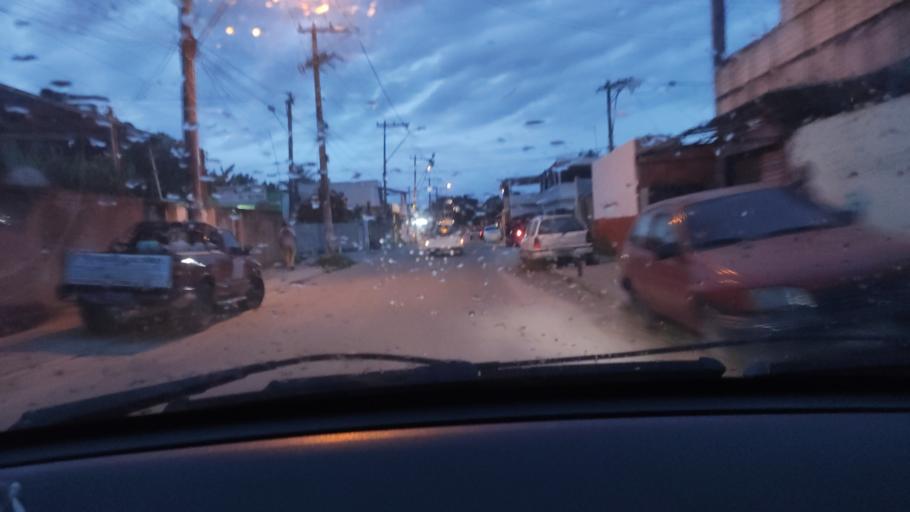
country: BR
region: Rio de Janeiro
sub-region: Itaborai
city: Itaborai
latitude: -22.7794
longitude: -42.9428
